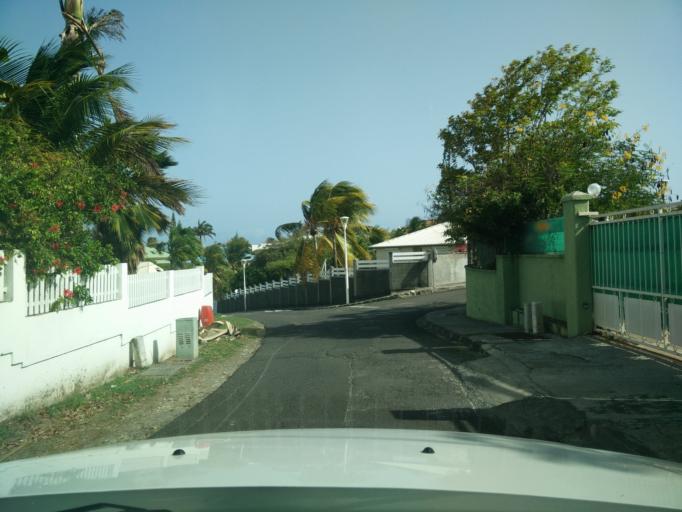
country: GP
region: Guadeloupe
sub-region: Guadeloupe
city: Le Gosier
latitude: 16.2013
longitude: -61.4717
